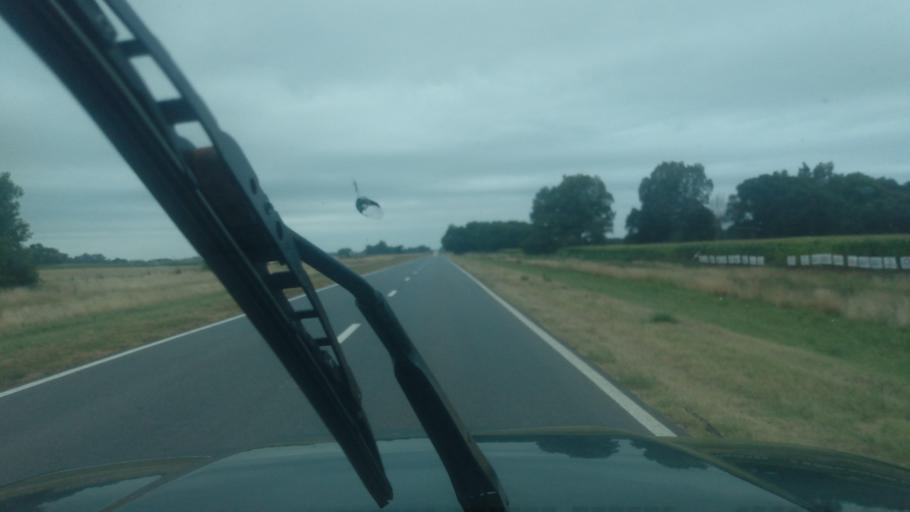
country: AR
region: Buenos Aires
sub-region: Partido de Bragado
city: Bragado
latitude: -35.2983
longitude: -60.6120
